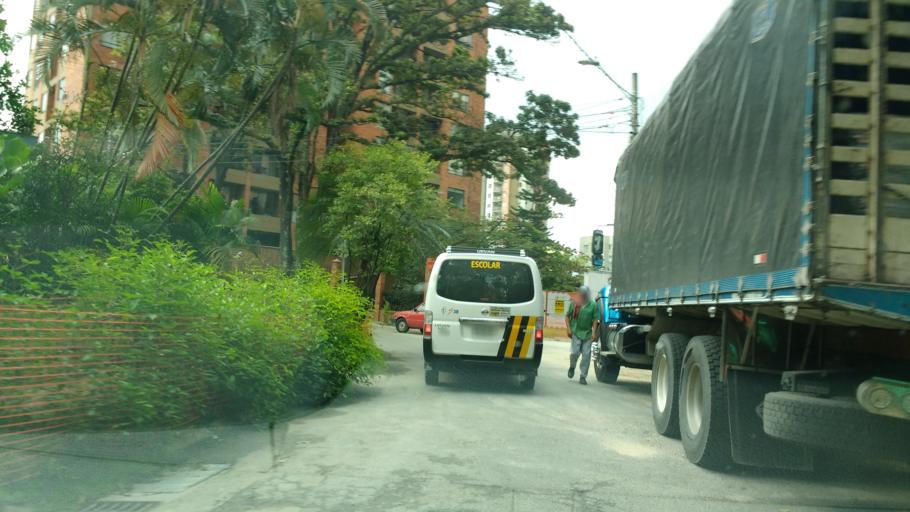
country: CO
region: Antioquia
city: Envigado
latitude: 6.1885
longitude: -75.5803
